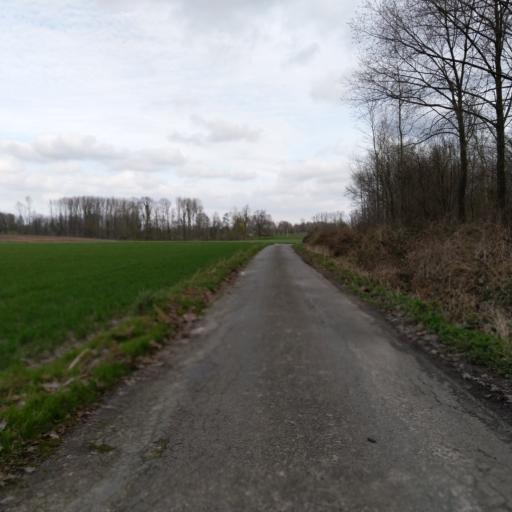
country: BE
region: Wallonia
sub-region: Province du Hainaut
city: Jurbise
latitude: 50.5299
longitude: 3.9889
